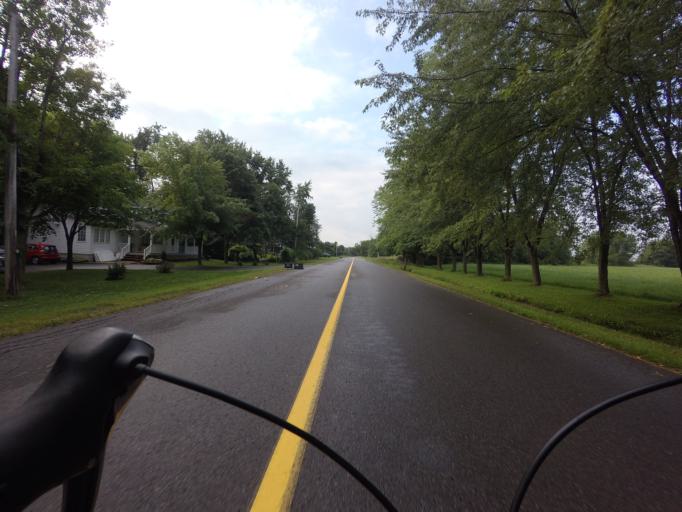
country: CA
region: Ontario
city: Bells Corners
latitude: 45.2398
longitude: -75.8087
